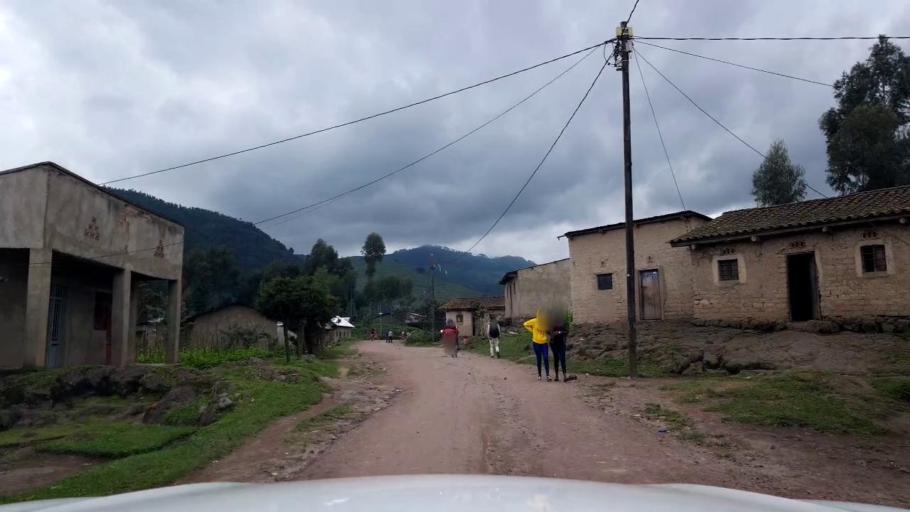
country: RW
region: Western Province
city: Gisenyi
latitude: -1.6373
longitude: 29.4057
